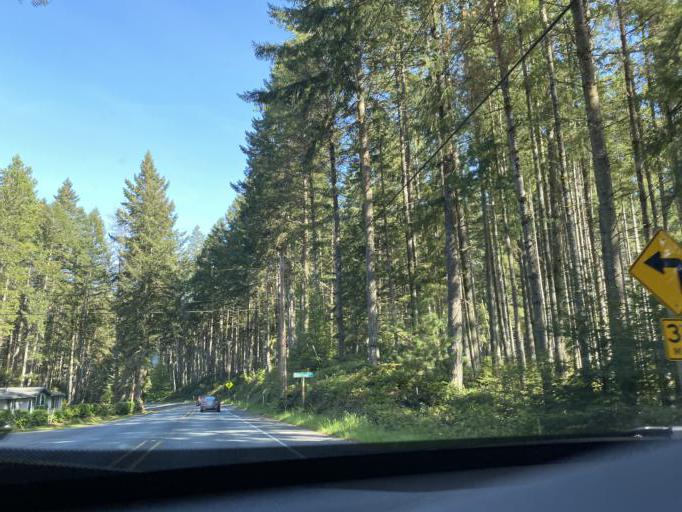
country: US
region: Washington
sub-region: Island County
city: Langley
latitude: 48.0319
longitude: -122.4358
